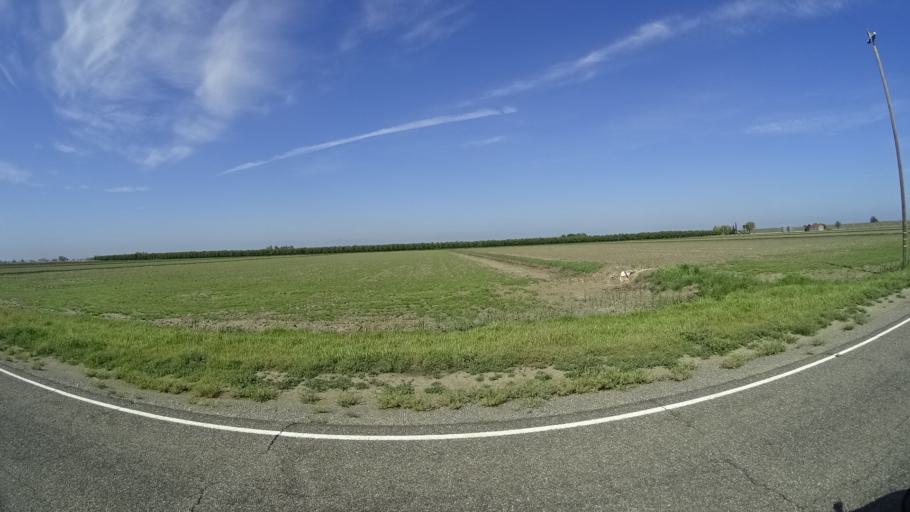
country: US
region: California
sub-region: Glenn County
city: Hamilton City
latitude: 39.6129
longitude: -122.0369
